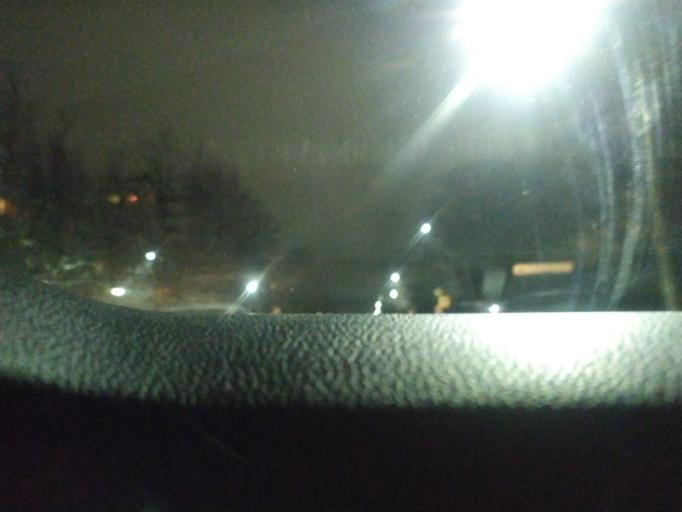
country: RU
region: Leningrad
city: Kirovsk
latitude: 59.8806
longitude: 30.9921
